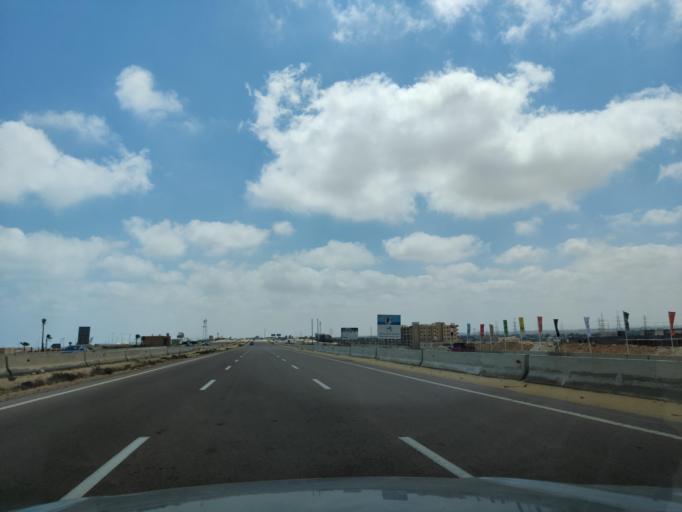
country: EG
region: Muhafazat Matruh
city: Al `Alamayn
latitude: 30.8238
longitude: 29.1860
